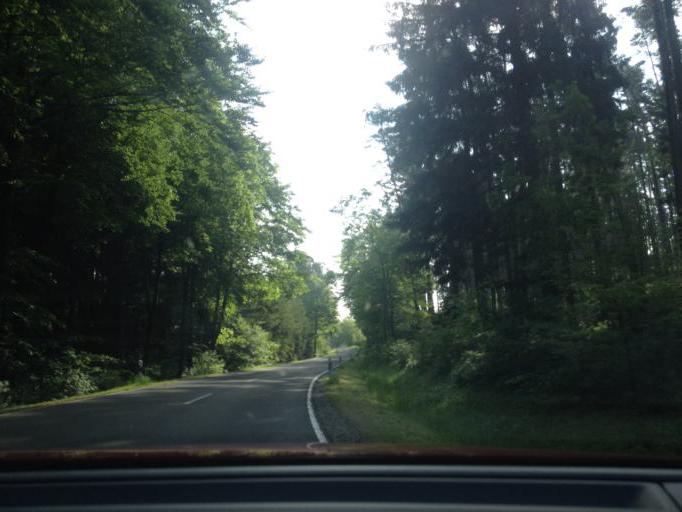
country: DE
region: Bavaria
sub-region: Upper Palatinate
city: Speinshart
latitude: 49.7946
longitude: 11.8372
